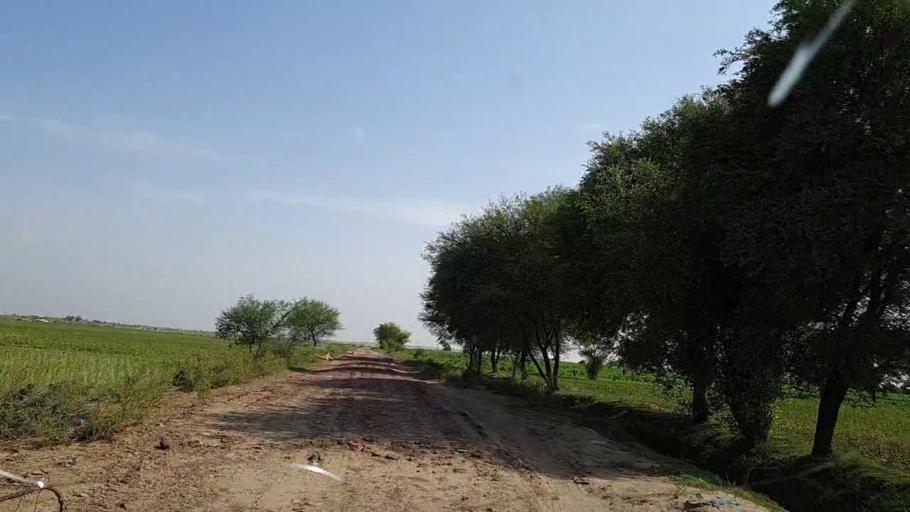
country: PK
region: Sindh
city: Khanpur
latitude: 27.6904
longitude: 69.3674
